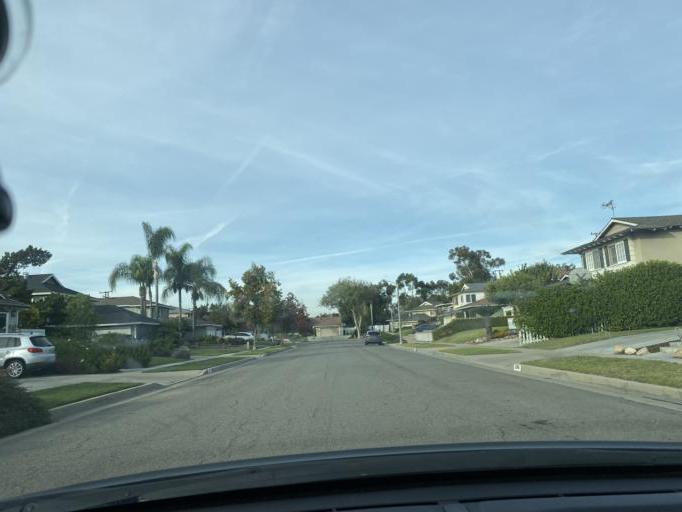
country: US
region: California
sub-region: Orange County
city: Brea
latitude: 33.8994
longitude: -117.8781
